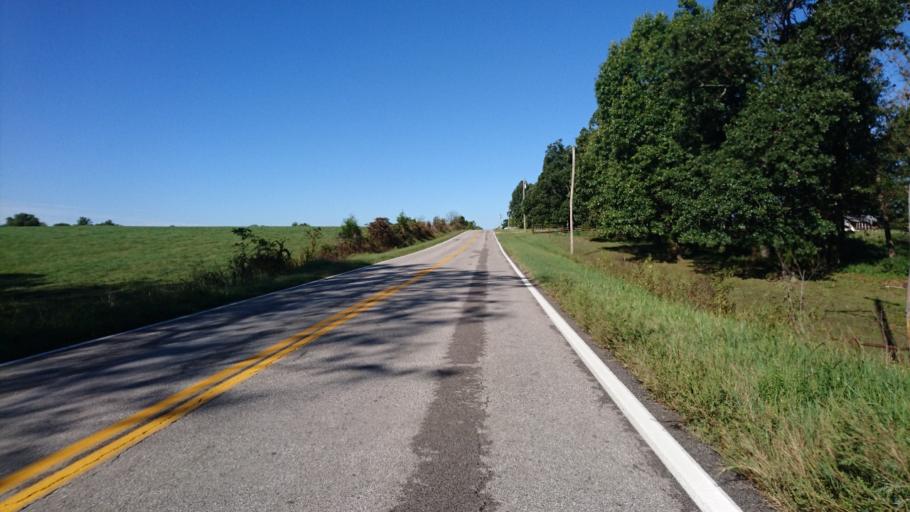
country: US
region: Missouri
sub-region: Greene County
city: Ash Grove
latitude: 37.1937
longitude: -93.6433
